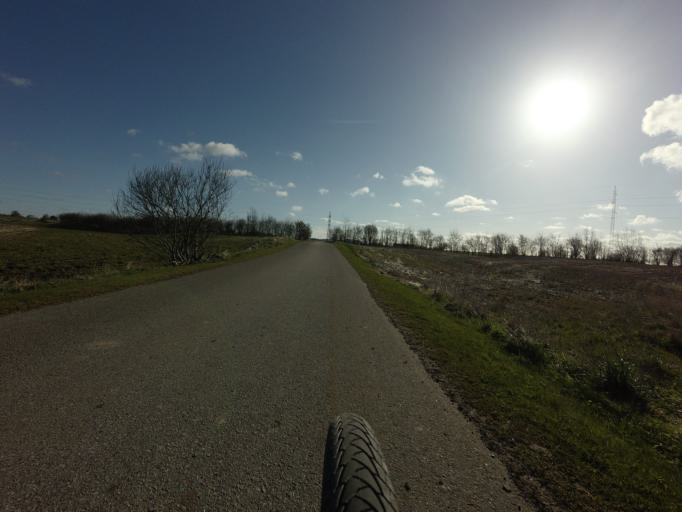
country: DK
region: North Denmark
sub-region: Hjorring Kommune
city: Vra
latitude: 57.3611
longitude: 9.8250
